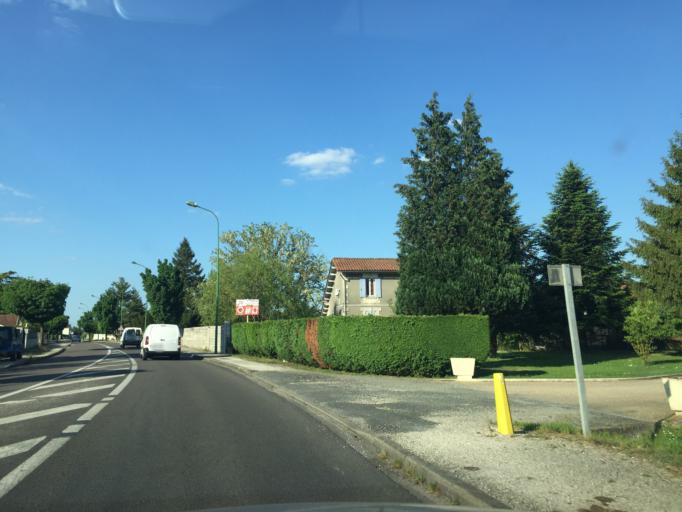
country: FR
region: Aquitaine
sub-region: Departement de la Gironde
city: Les Eglisottes-et-Chalaures
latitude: 45.0905
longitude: -0.0464
